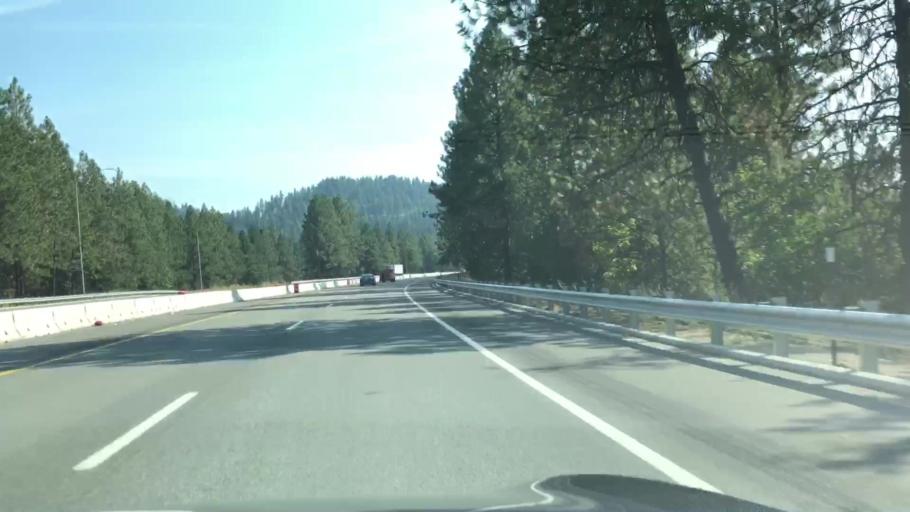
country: US
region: Idaho
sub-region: Kootenai County
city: Coeur d'Alene
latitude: 47.6765
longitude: -116.7530
